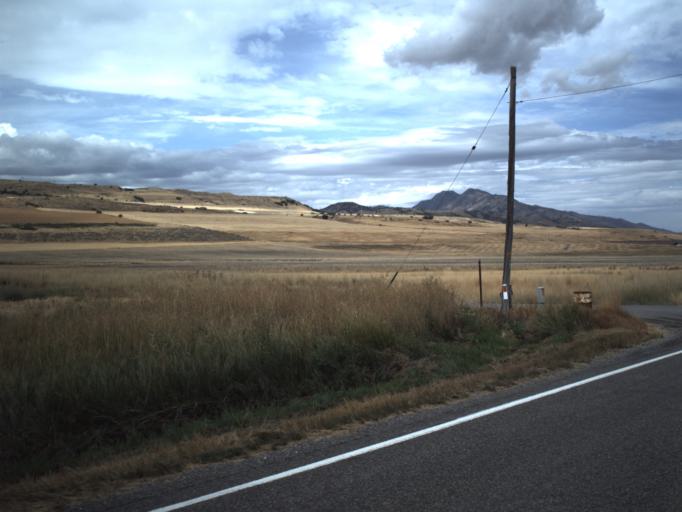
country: US
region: Utah
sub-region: Cache County
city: Benson
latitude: 41.8248
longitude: -111.9997
